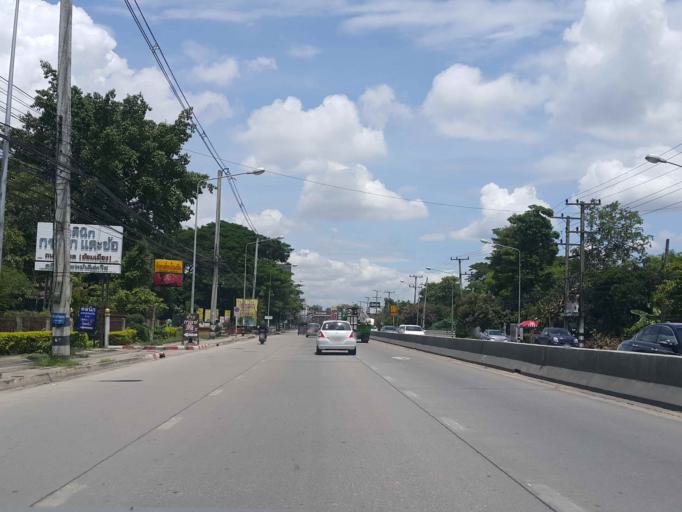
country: TH
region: Chiang Mai
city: Chiang Mai
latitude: 18.7668
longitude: 98.9867
